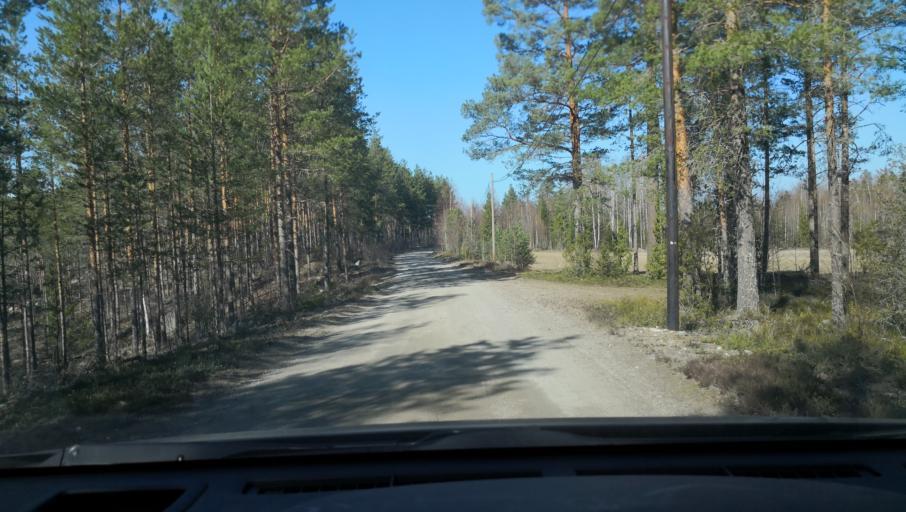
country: SE
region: Vaestmanland
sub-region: Sala Kommun
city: Sala
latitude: 59.9282
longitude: 16.4494
